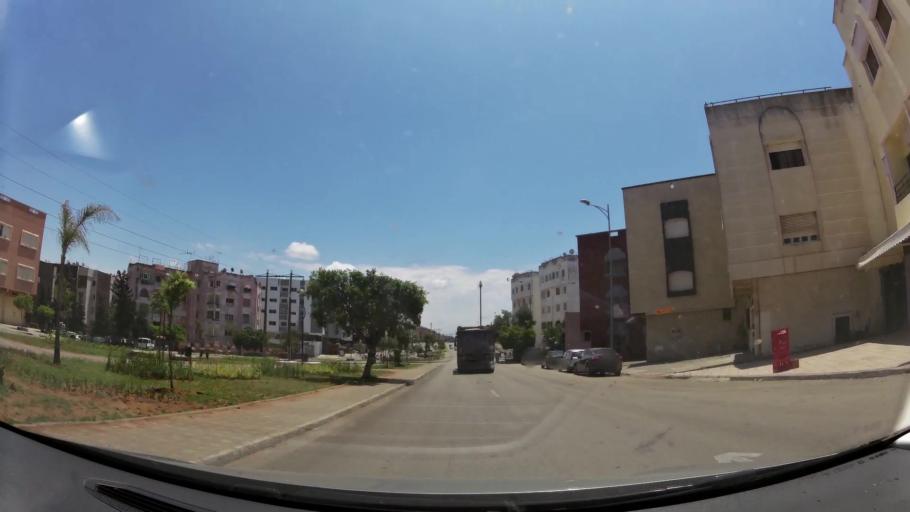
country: MA
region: Gharb-Chrarda-Beni Hssen
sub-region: Kenitra Province
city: Kenitra
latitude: 34.2584
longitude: -6.6162
